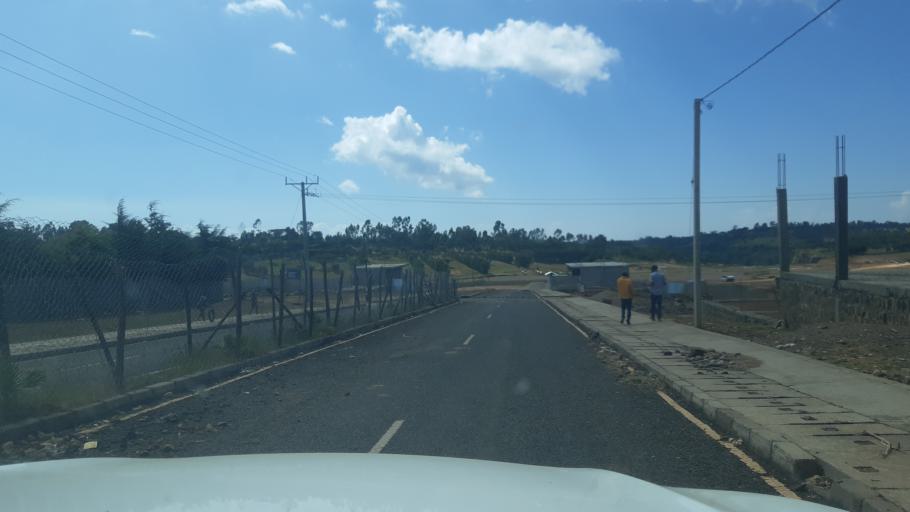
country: ET
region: Amhara
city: Dabat
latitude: 13.3905
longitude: 37.3997
